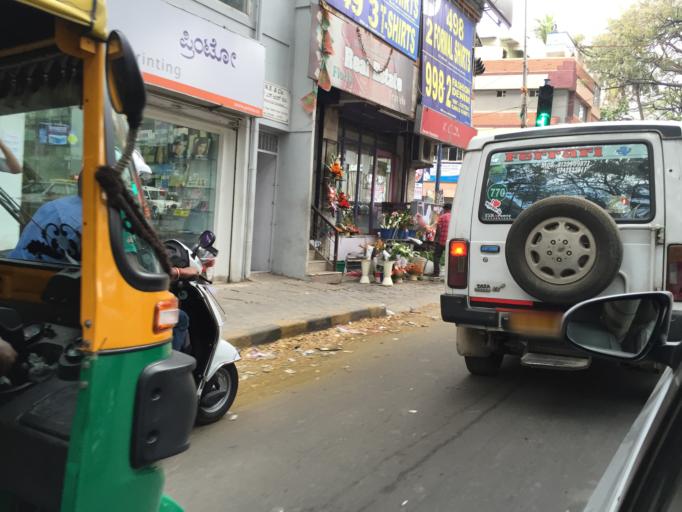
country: IN
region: Karnataka
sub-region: Bangalore Urban
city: Bangalore
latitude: 12.9780
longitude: 77.6366
